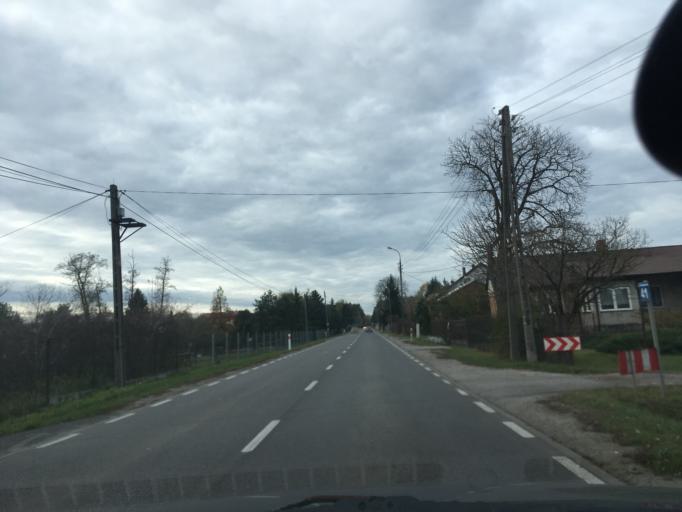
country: PL
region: Masovian Voivodeship
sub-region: Powiat piaseczynski
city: Tarczyn
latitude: 51.9789
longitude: 20.8758
